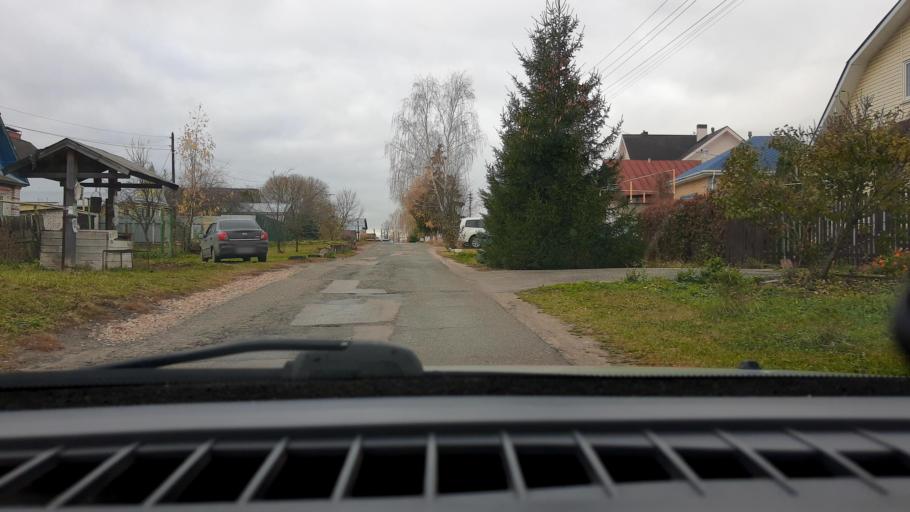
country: RU
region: Nizjnij Novgorod
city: Afonino
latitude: 56.1918
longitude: 44.0871
